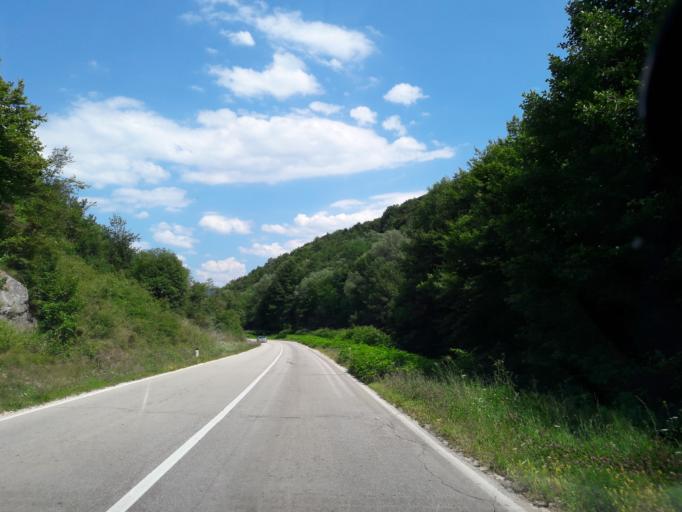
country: BA
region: Republika Srpska
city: Mrkonjic Grad
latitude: 44.4239
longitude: 17.1257
